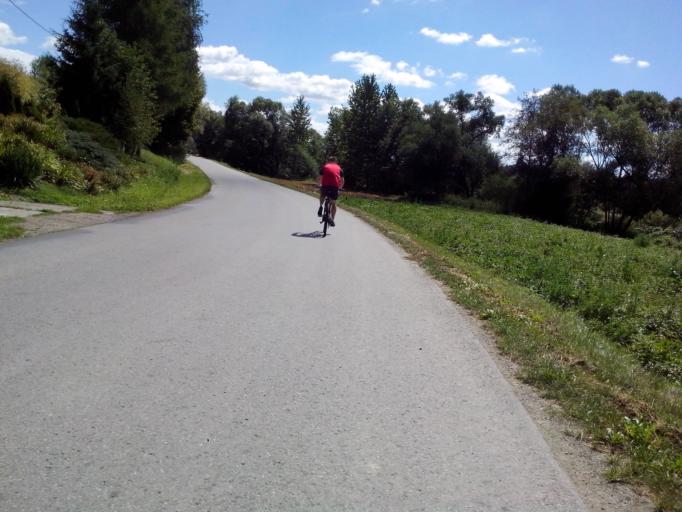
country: PL
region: Subcarpathian Voivodeship
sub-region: Powiat brzozowski
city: Domaradz
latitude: 49.7893
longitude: 21.9802
